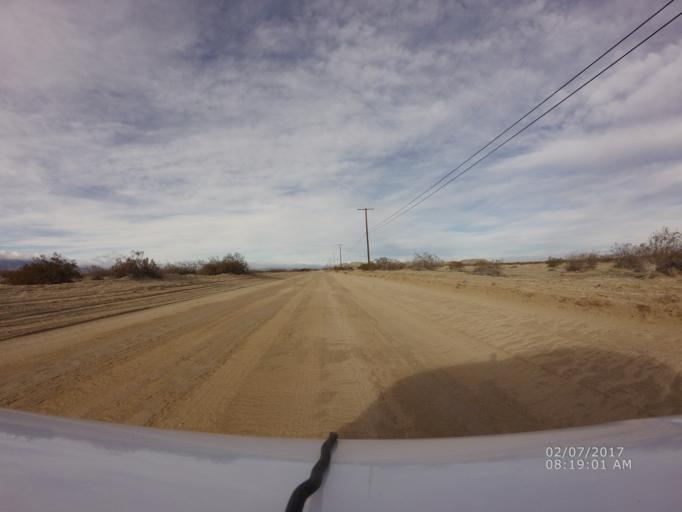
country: US
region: California
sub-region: Los Angeles County
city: Lake Los Angeles
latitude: 34.5873
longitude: -117.7776
